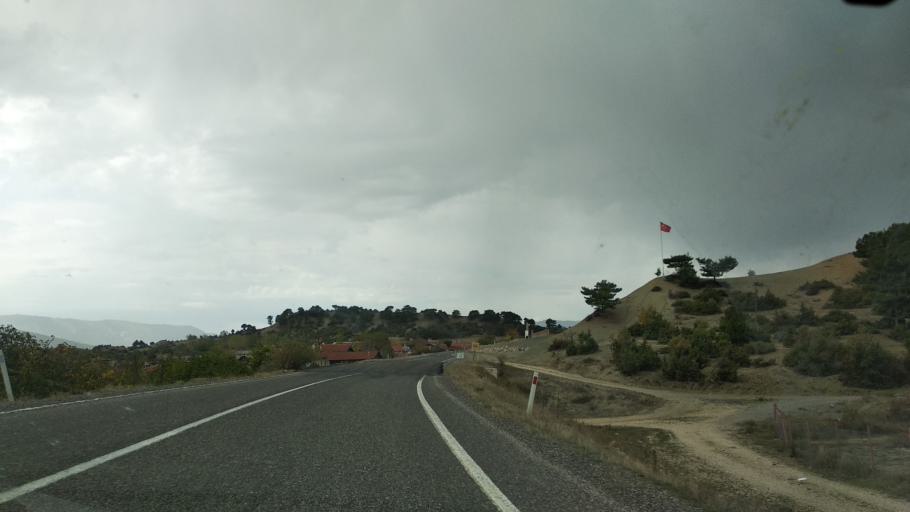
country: TR
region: Bolu
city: Seben
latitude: 40.3339
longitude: 31.4676
